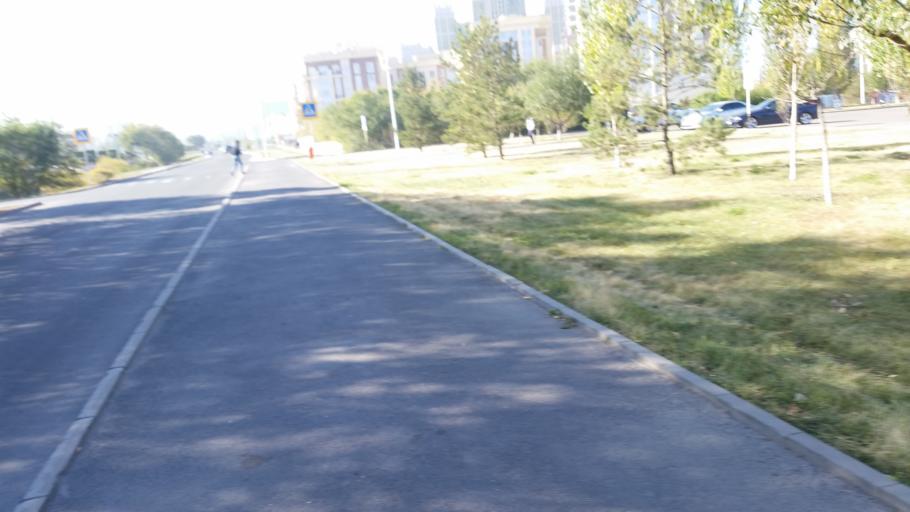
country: KZ
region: Astana Qalasy
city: Astana
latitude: 51.1442
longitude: 71.4200
